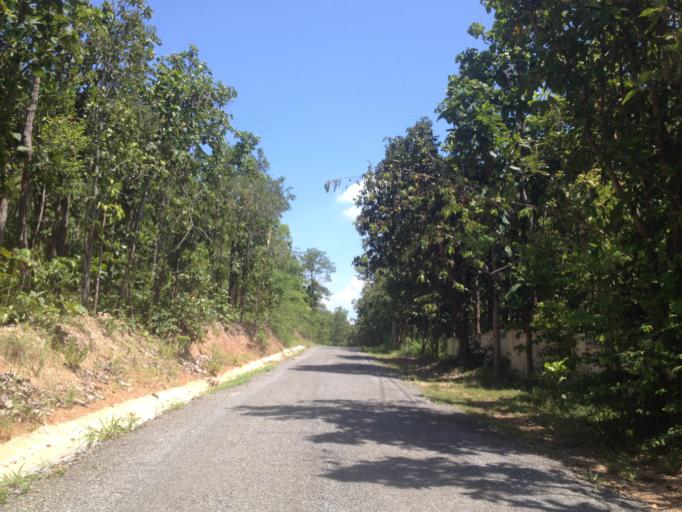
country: TH
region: Chiang Mai
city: Hang Dong
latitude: 18.7318
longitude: 98.9128
